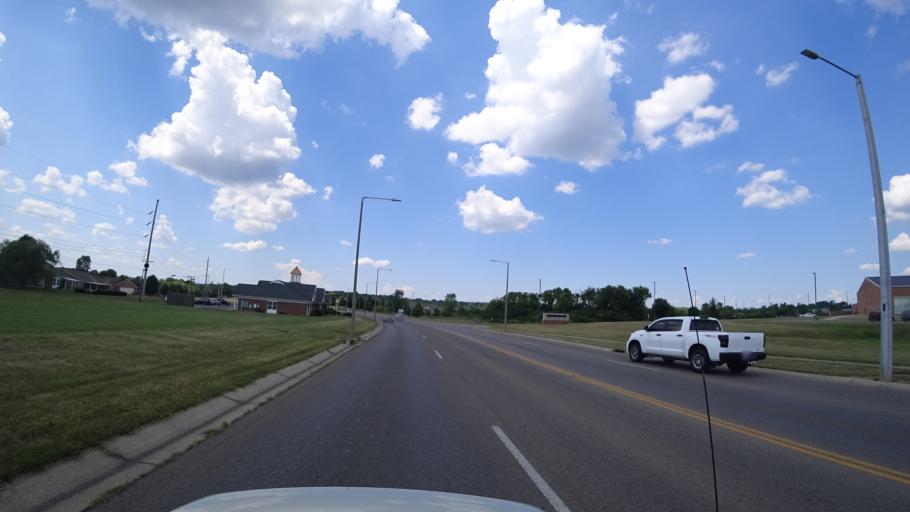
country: US
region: Ohio
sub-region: Butler County
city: New Miami
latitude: 39.4222
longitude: -84.5545
